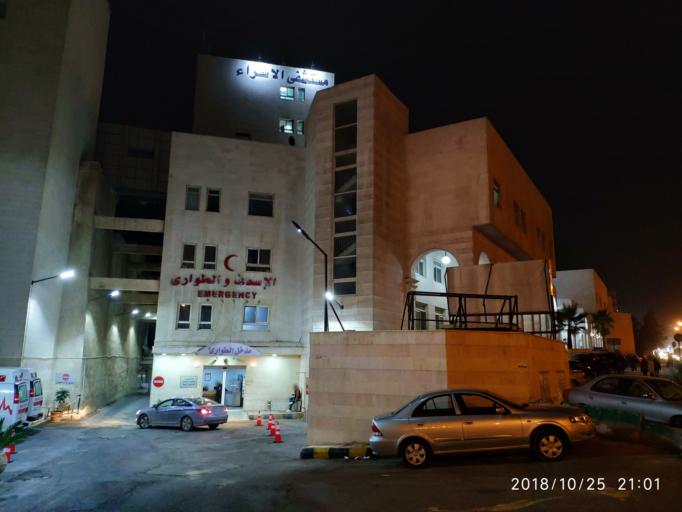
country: JO
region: Amman
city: Al Jubayhah
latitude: 32.0167
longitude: 35.8666
